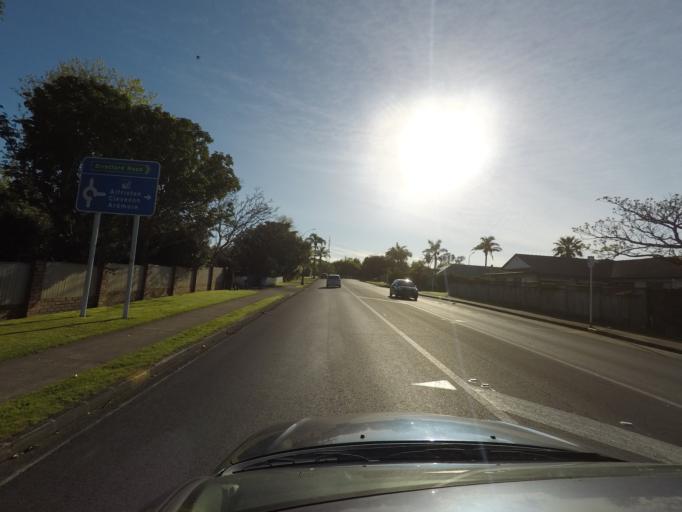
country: NZ
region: Auckland
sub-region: Auckland
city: Takanini
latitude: -37.0119
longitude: 174.9140
